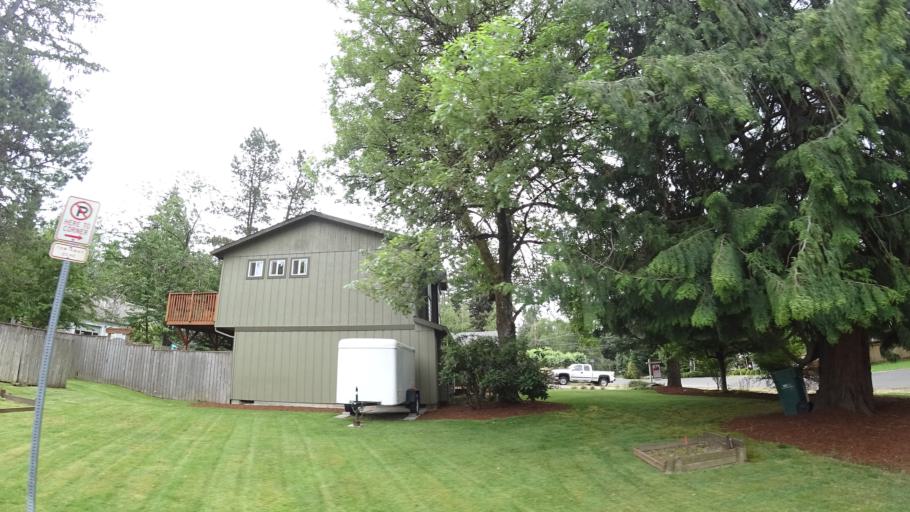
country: US
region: Oregon
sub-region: Washington County
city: Garden Home-Whitford
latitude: 45.4635
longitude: -122.7657
